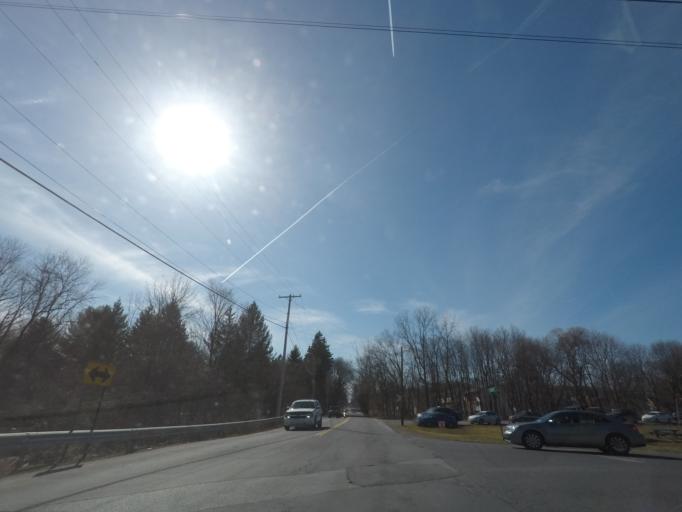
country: US
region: New York
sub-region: Saratoga County
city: Ballston Spa
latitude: 43.0014
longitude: -73.8403
